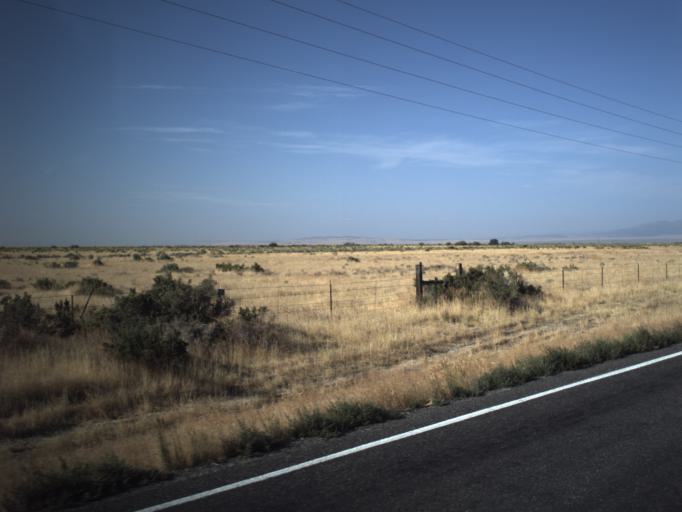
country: US
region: Idaho
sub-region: Oneida County
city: Malad City
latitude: 41.9669
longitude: -112.7905
